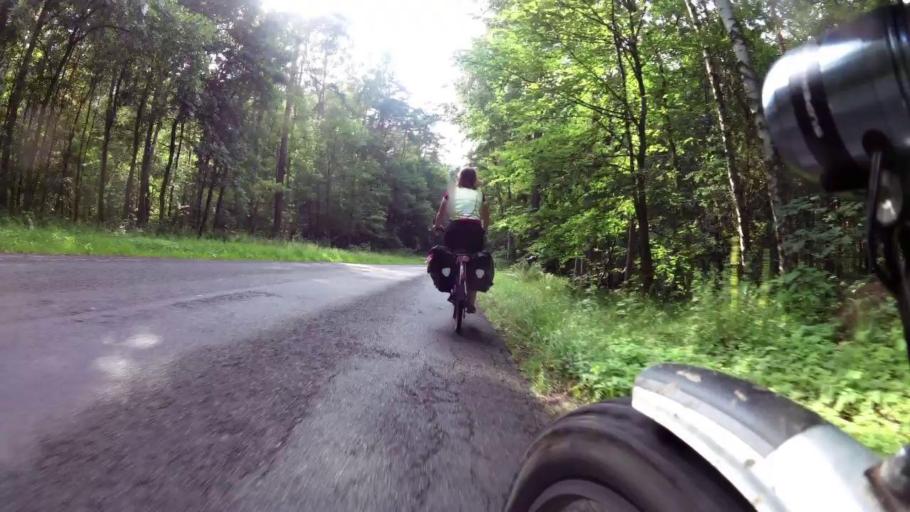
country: PL
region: West Pomeranian Voivodeship
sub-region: Powiat gryfinski
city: Gryfino
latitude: 53.2319
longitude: 14.5400
